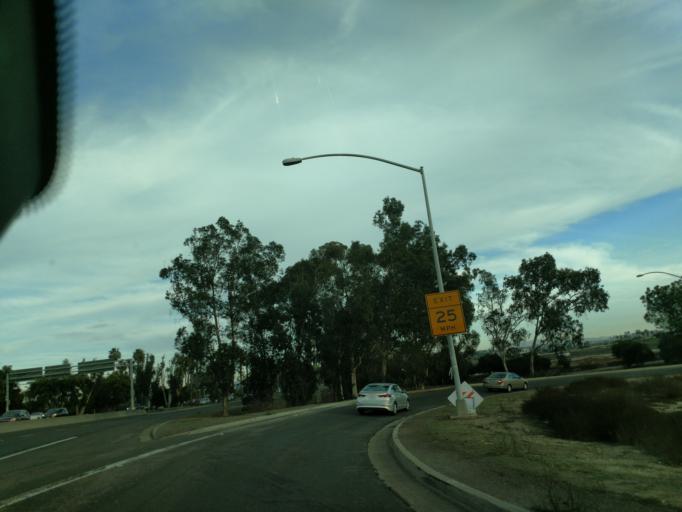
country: US
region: California
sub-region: San Diego County
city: San Diego
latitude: 32.7617
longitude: -117.2290
